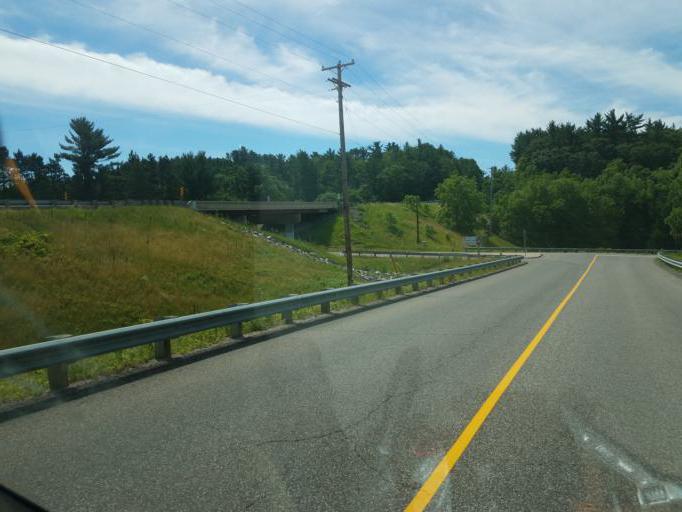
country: US
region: Wisconsin
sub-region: Columbia County
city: Wisconsin Dells
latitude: 43.6407
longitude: -89.7641
